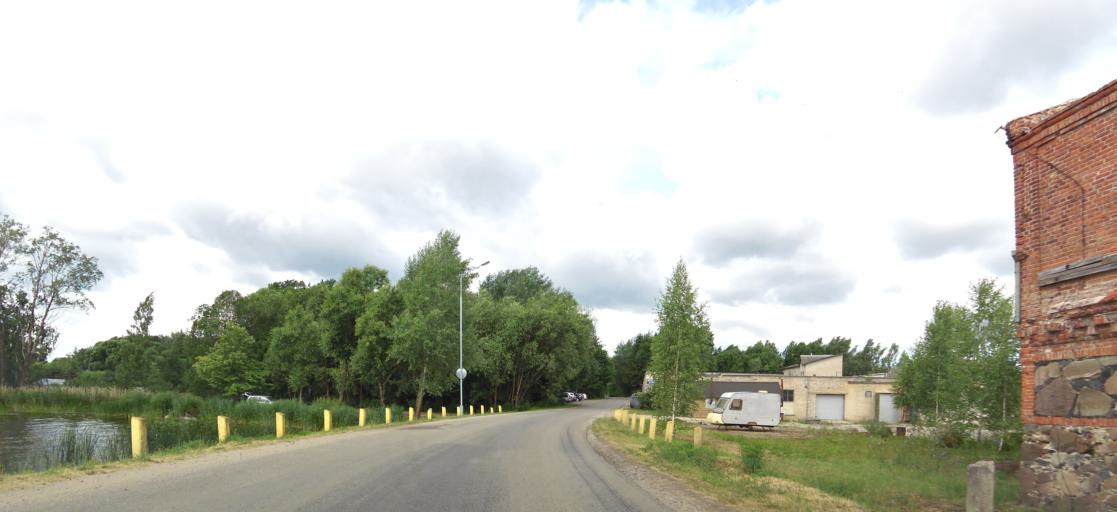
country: LT
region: Panevezys
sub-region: Birzai
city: Birzai
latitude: 56.2218
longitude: 24.7583
